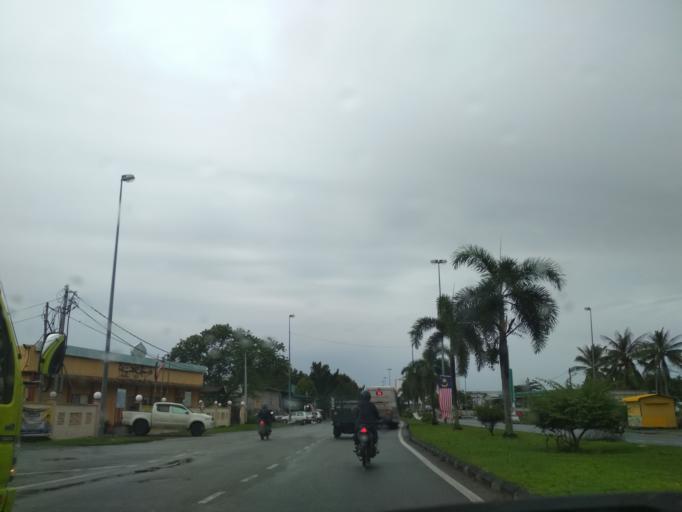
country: MY
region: Perlis
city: Kangar
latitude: 6.4274
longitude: 100.1848
